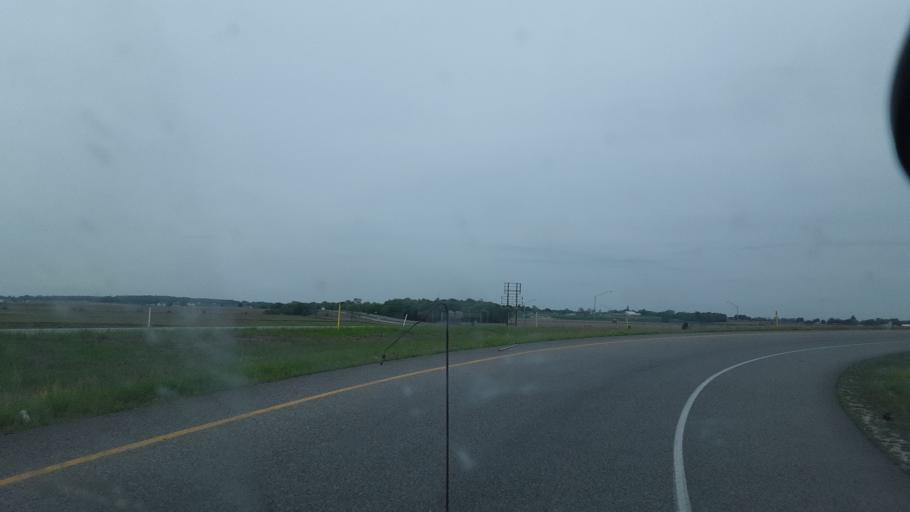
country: US
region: Indiana
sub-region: Gibson County
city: Haubstadt
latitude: 38.1657
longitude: -87.5519
